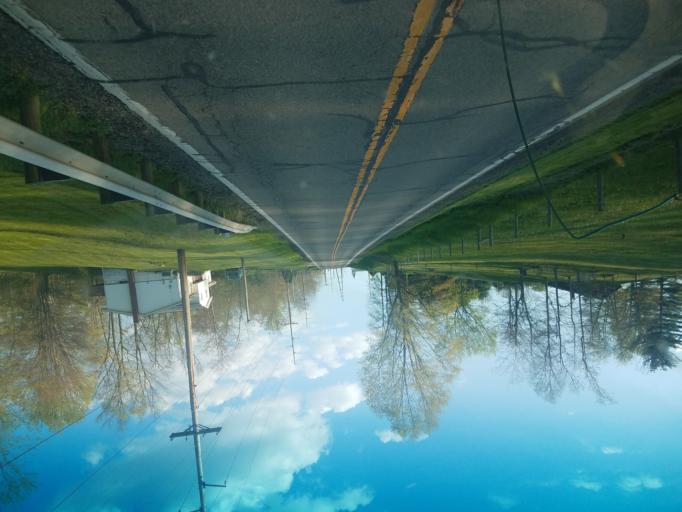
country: US
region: Ohio
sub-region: Wayne County
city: Shreve
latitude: 40.6012
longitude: -82.0244
